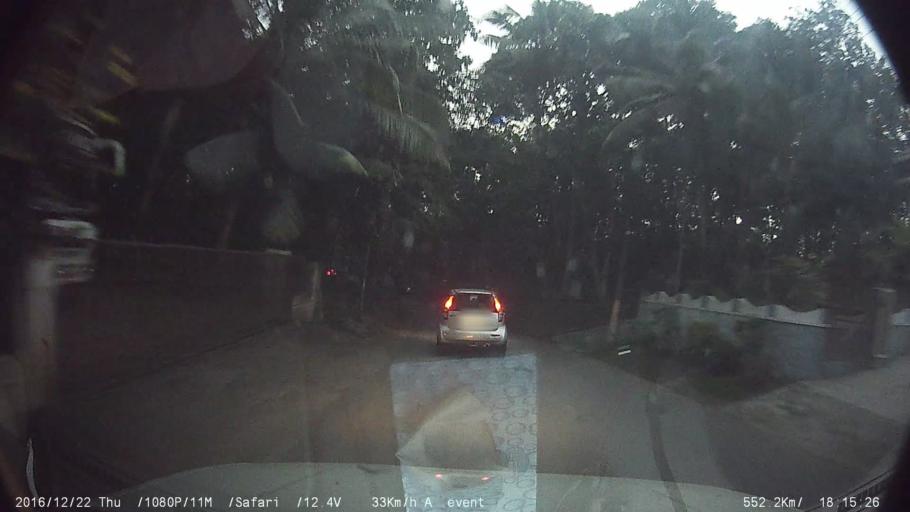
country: IN
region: Kerala
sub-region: Kottayam
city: Palackattumala
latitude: 9.7736
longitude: 76.6118
